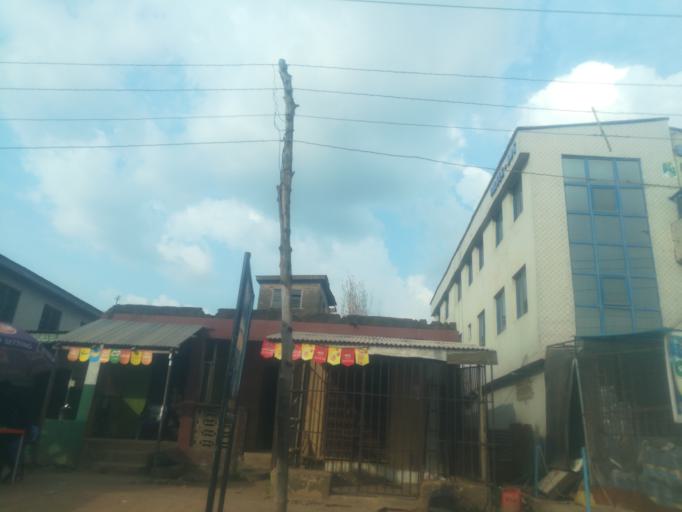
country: NG
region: Ogun
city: Abeokuta
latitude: 7.1486
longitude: 3.3132
